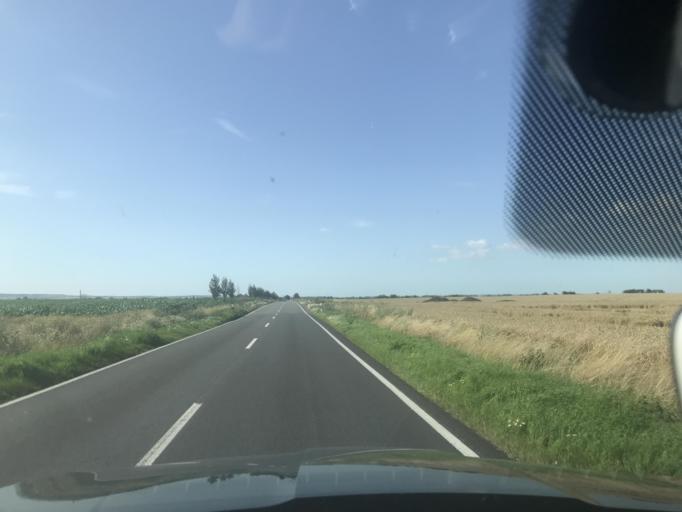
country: DE
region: Saxony-Anhalt
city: Wegeleben
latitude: 51.8597
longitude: 11.1863
